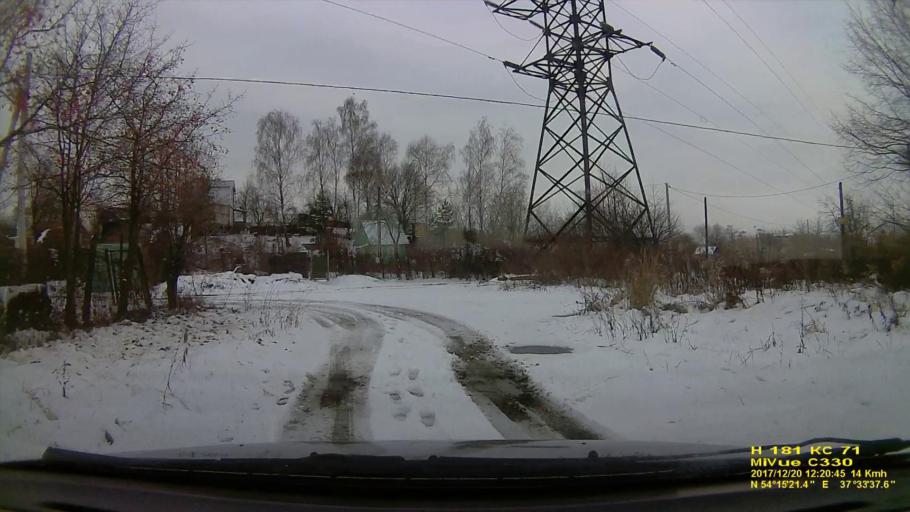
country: RU
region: Tula
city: Gorelki
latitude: 54.2559
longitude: 37.5605
